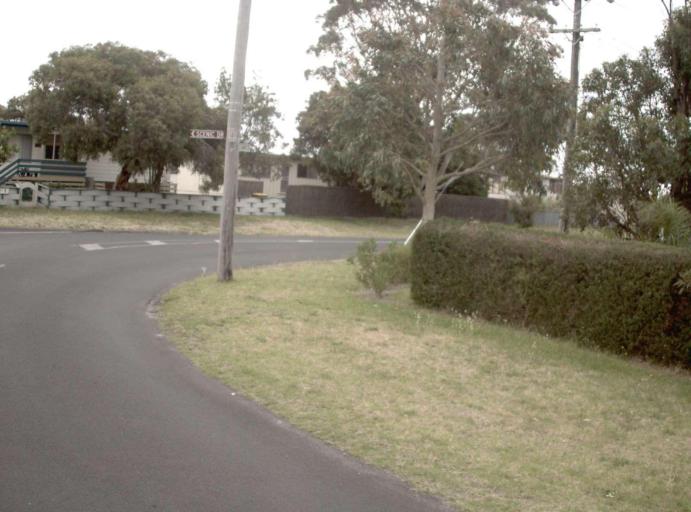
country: AU
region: Victoria
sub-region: East Gippsland
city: Bairnsdale
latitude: -38.0536
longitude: 147.5730
